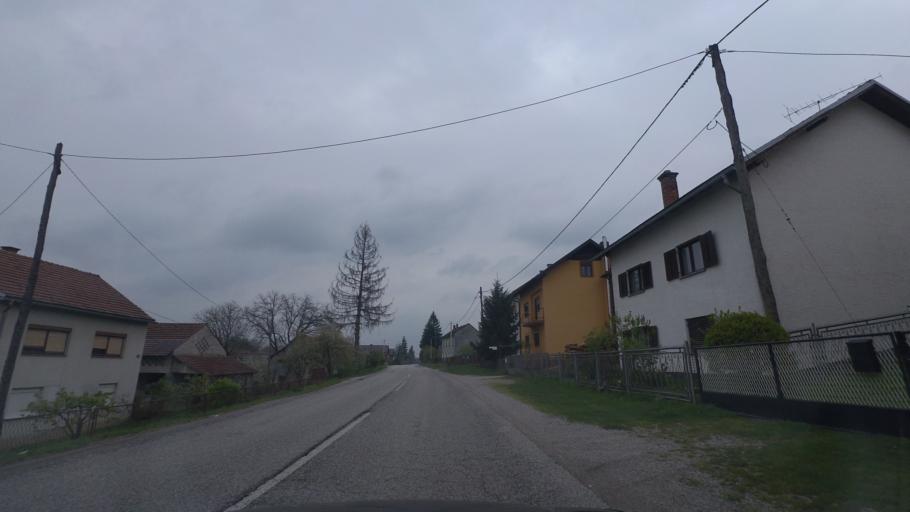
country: HR
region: Karlovacka
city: Ozalj
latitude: 45.6365
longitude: 15.5392
